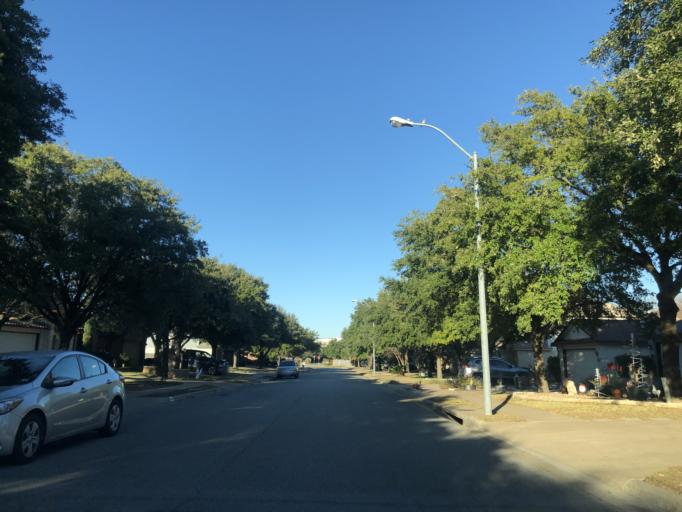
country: US
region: Texas
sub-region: Travis County
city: Windemere
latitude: 30.4798
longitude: -97.6552
